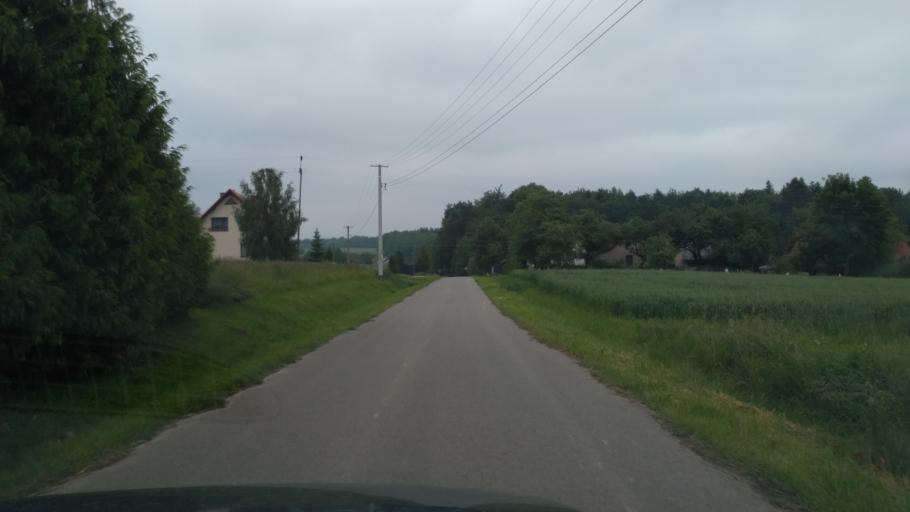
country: PL
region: Subcarpathian Voivodeship
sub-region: Powiat ropczycko-sedziszowski
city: Zagorzyce
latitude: 49.9895
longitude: 21.7060
